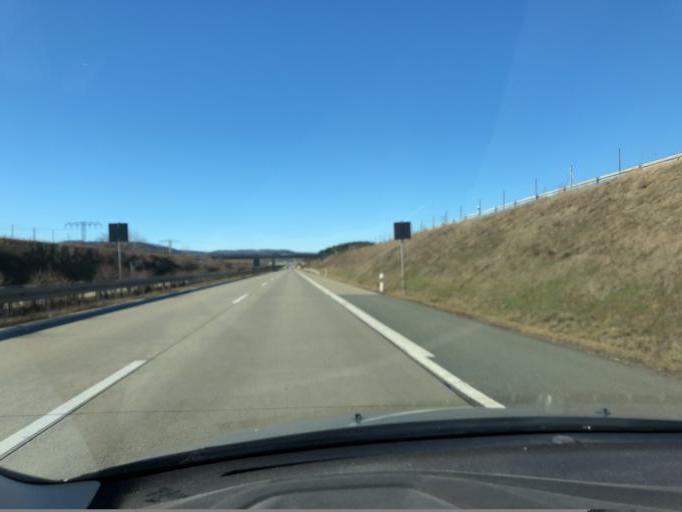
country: DE
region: Saxony-Anhalt
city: Timmenrode
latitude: 51.8051
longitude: 10.9909
